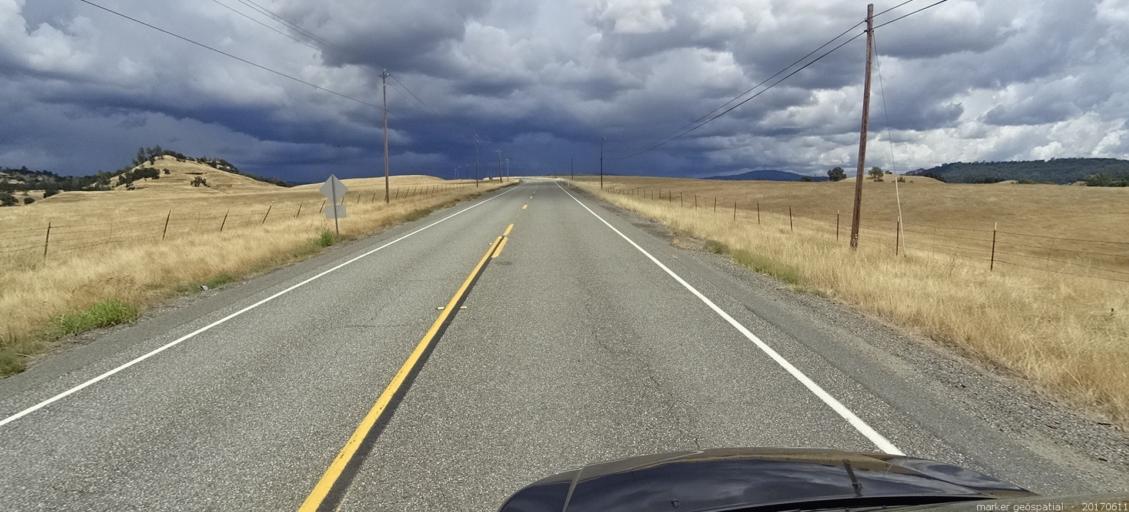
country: US
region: California
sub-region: Butte County
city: Paradise
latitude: 39.6478
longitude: -121.6068
